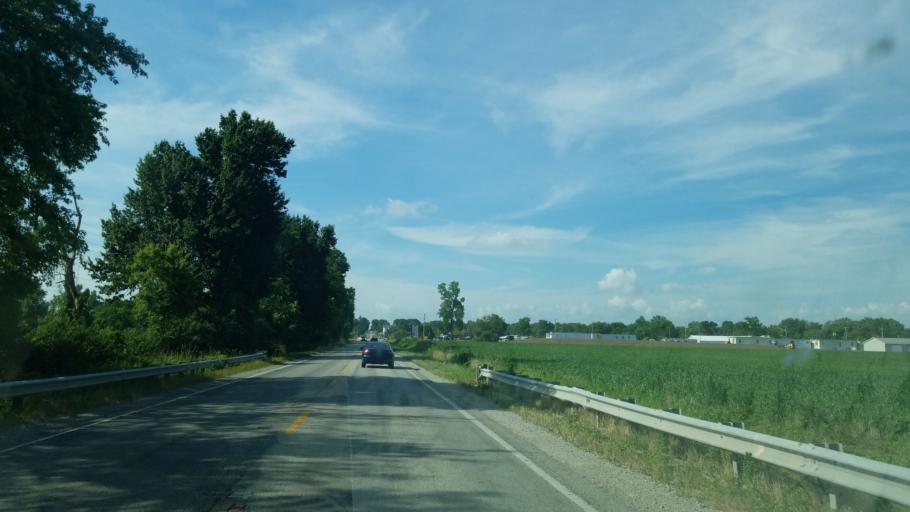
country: US
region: Illinois
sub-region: Saint Clair County
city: Lebanon
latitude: 38.5905
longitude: -89.8077
